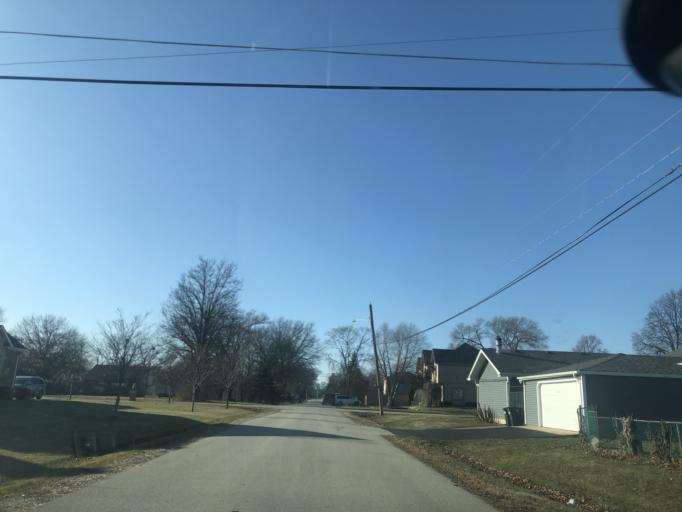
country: US
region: Illinois
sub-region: DuPage County
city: Addison
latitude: 41.9377
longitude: -88.0109
